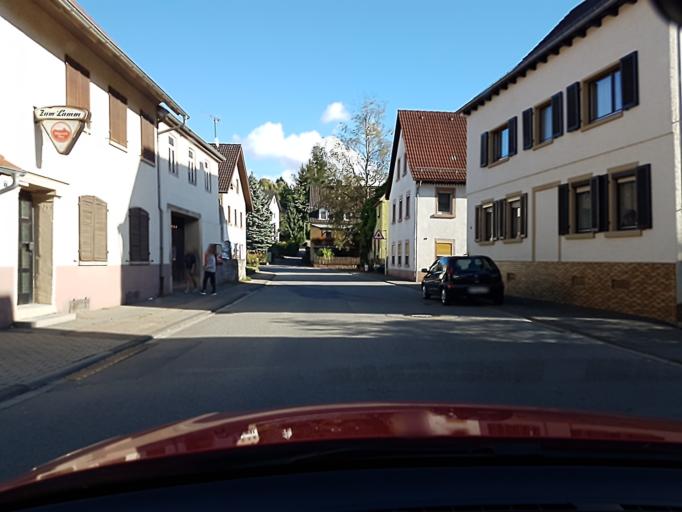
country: DE
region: Baden-Wuerttemberg
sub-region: Karlsruhe Region
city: Spechbach
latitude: 49.3460
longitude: 8.8849
